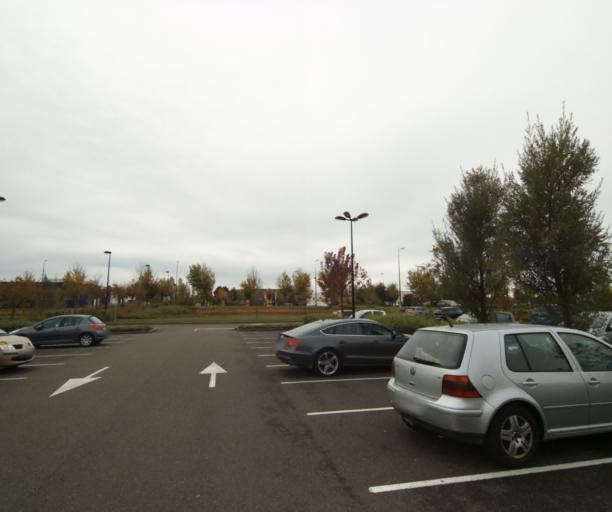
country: FR
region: Centre
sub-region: Departement d'Eure-et-Loir
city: Dreux
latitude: 48.7510
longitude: 1.3505
